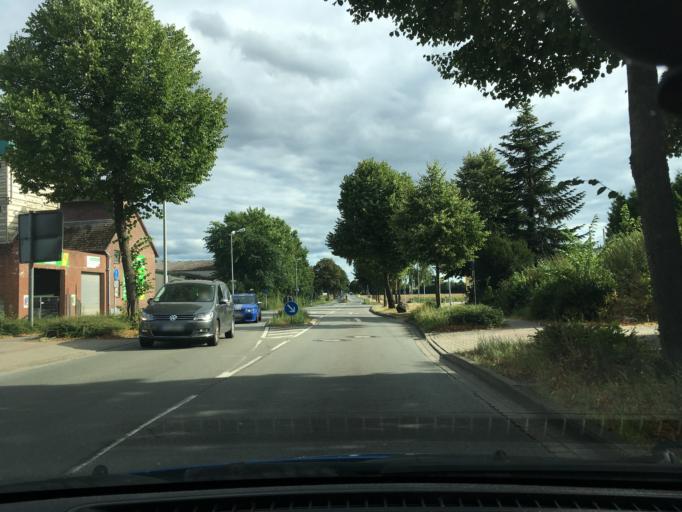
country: DE
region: Lower Saxony
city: Neu Wulmstorf
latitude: 53.4234
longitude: 9.7896
